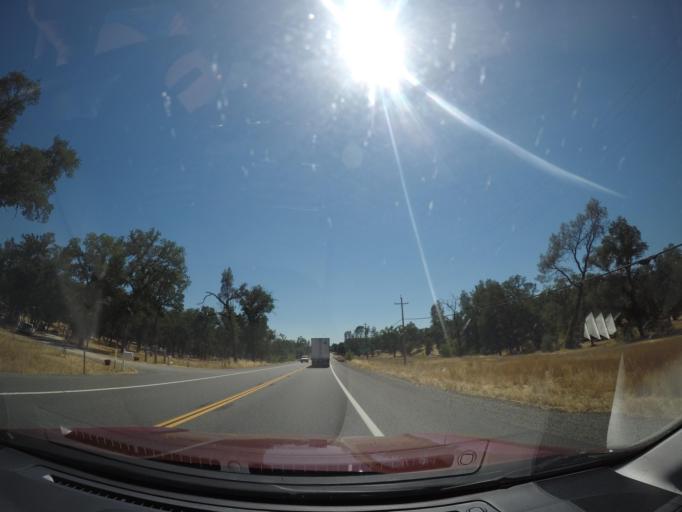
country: US
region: California
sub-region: Shasta County
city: Bella Vista
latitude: 40.6436
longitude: -122.2274
